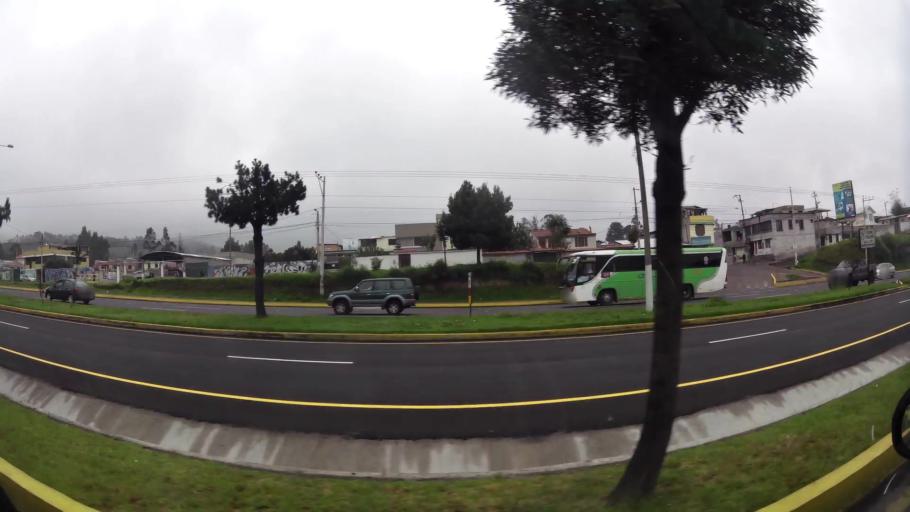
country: EC
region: Pichincha
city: Sangolqui
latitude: -0.2789
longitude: -78.4803
